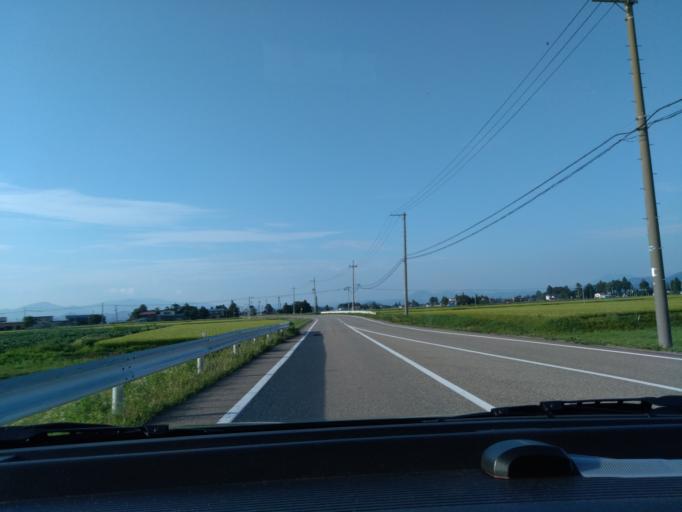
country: JP
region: Akita
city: Kakunodatemachi
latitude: 39.5168
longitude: 140.5585
